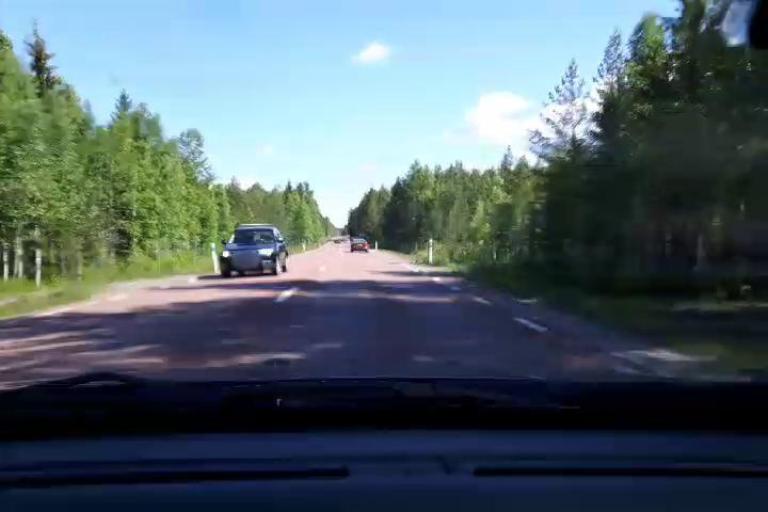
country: SE
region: Gaevleborg
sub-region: Hudiksvalls Kommun
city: Delsbo
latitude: 61.7923
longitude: 16.5865
